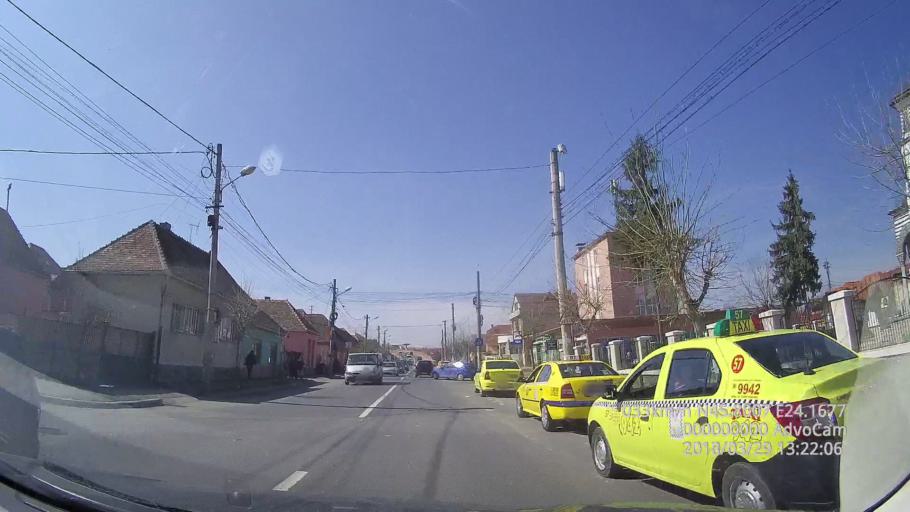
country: RO
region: Sibiu
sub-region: Municipiul Sibiu
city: Sibiu
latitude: 45.8006
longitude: 24.1675
